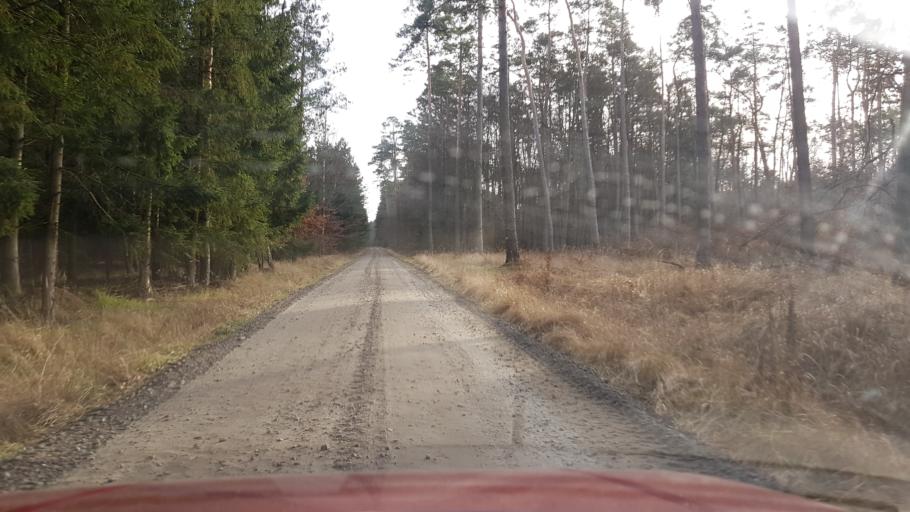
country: PL
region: West Pomeranian Voivodeship
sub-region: Powiat choszczenski
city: Pelczyce
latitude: 52.9213
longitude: 15.3689
